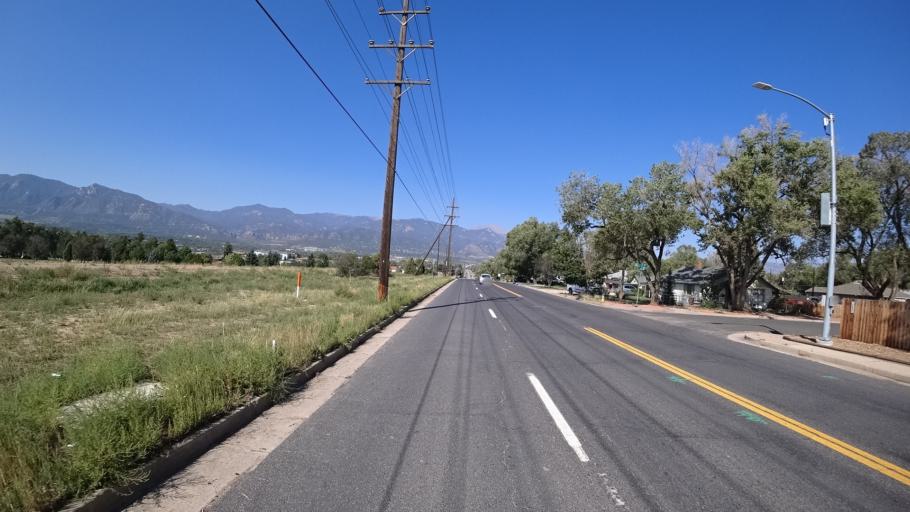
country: US
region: Colorado
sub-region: El Paso County
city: Colorado Springs
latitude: 38.8210
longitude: -104.8011
